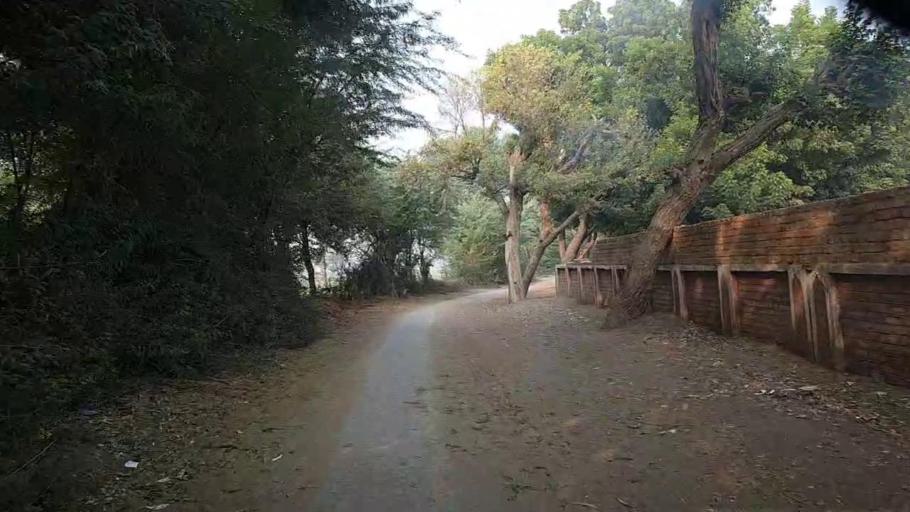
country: PK
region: Sindh
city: Bozdar
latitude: 27.1377
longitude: 68.6618
